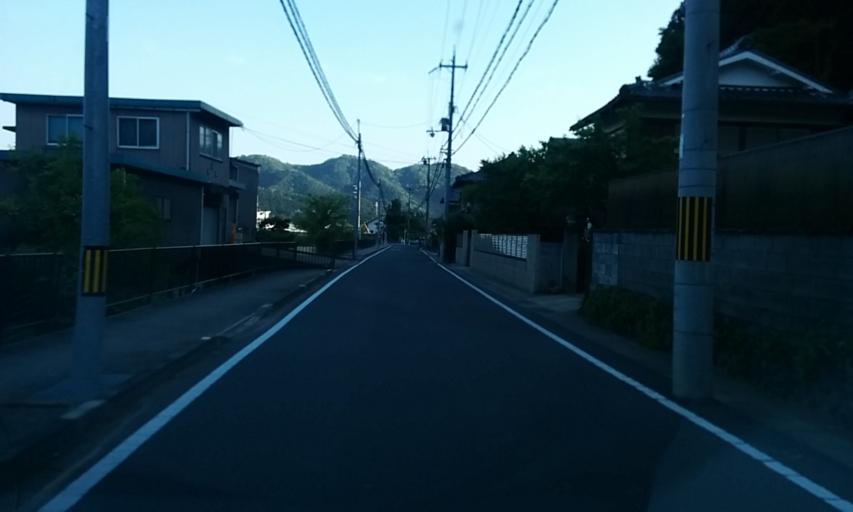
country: JP
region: Kyoto
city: Kameoka
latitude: 35.0829
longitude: 135.5167
